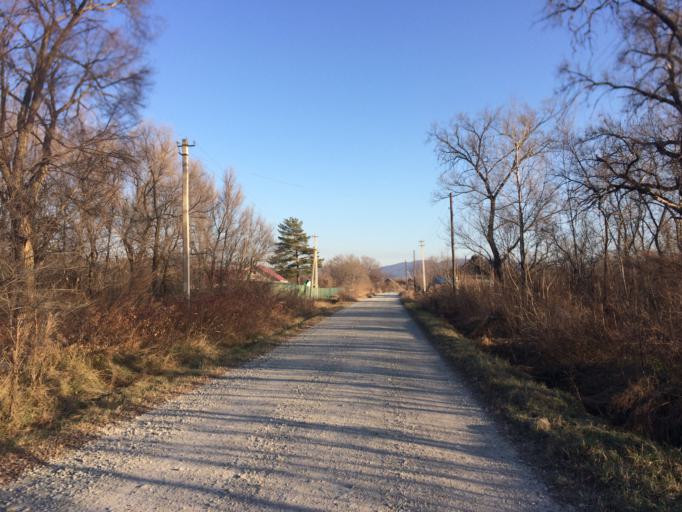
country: RU
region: Primorskiy
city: Ivanovka
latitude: 43.9563
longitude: 132.4811
